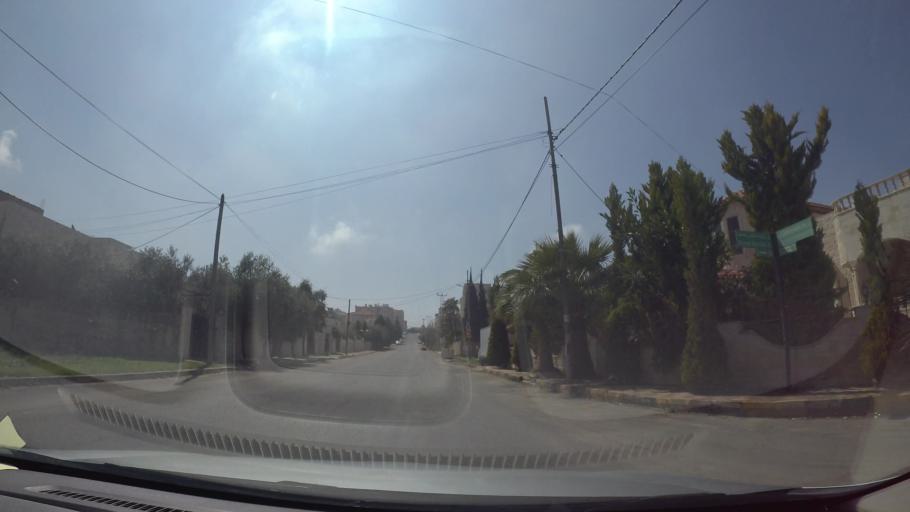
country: JO
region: Amman
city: Al Bunayyat ash Shamaliyah
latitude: 31.9004
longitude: 35.8882
